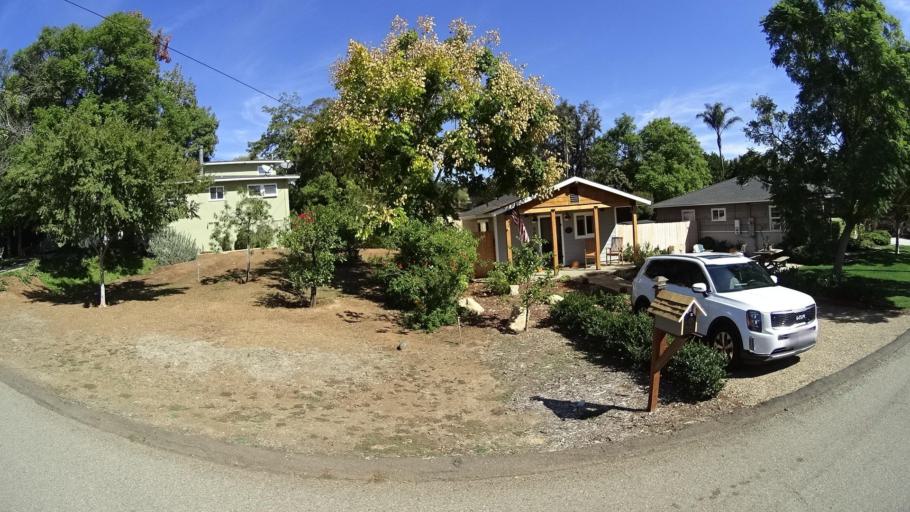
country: US
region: California
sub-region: San Diego County
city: Casa de Oro-Mount Helix
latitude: 32.7521
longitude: -116.9640
